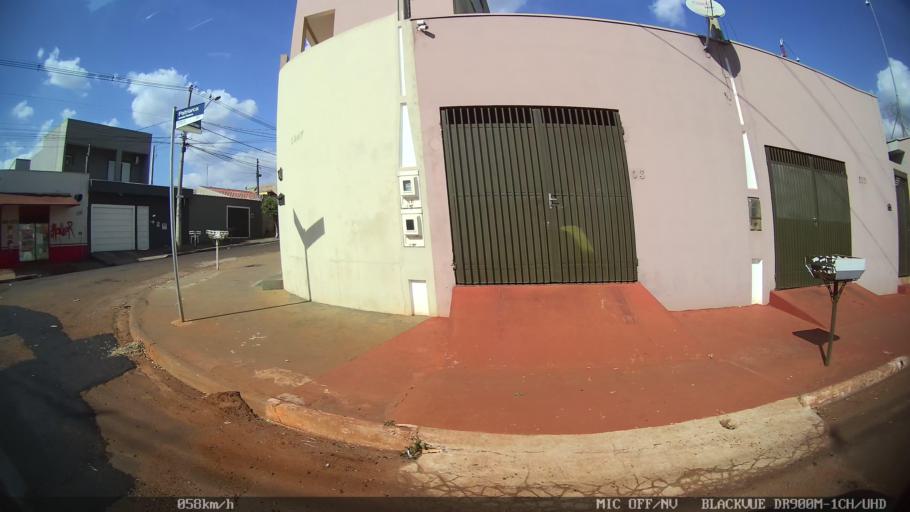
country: BR
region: Sao Paulo
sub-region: Ribeirao Preto
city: Ribeirao Preto
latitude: -21.2037
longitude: -47.8586
